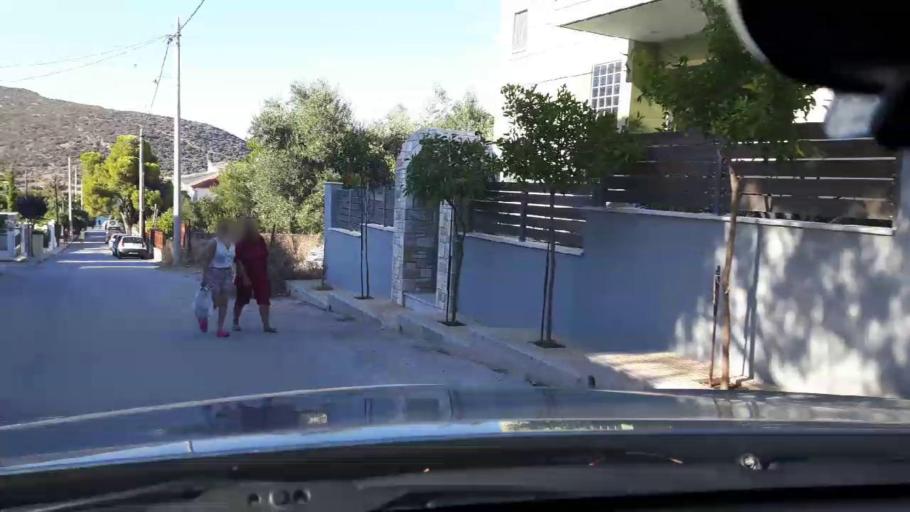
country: GR
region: Attica
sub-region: Nomarchia Anatolikis Attikis
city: Limin Mesoyaias
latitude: 37.8614
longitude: 24.0398
